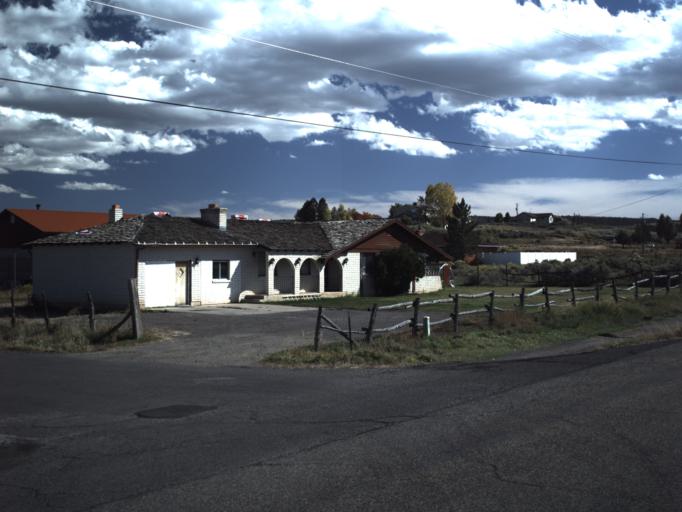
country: US
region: Utah
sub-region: Garfield County
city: Panguitch
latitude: 37.8100
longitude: -112.4354
